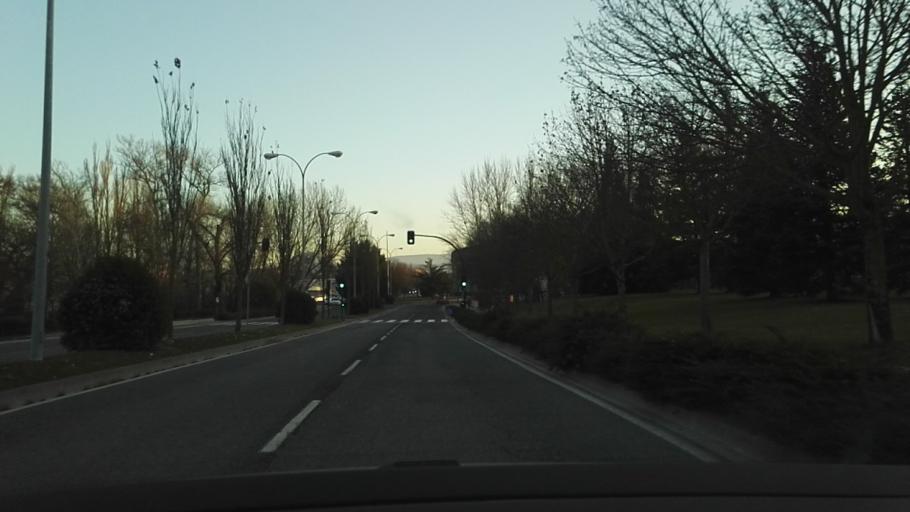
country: ES
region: Navarre
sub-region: Provincia de Navarra
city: Segundo Ensanche
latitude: 42.7979
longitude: -1.6322
